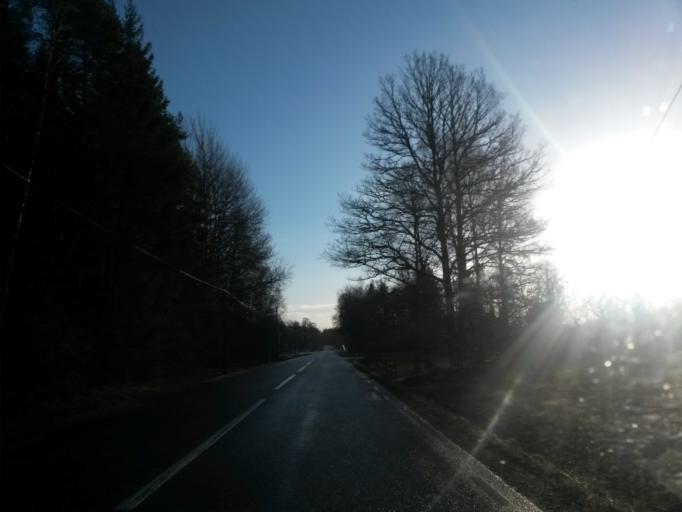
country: SE
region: Vaestra Goetaland
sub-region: Vargarda Kommun
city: Vargarda
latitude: 57.9332
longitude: 12.8544
